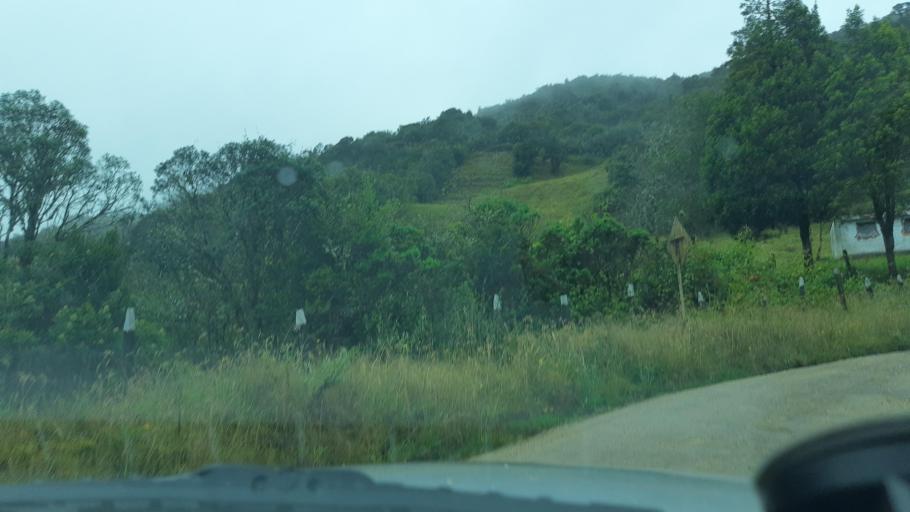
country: CO
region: Cundinamarca
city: Umbita
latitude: 5.2156
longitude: -73.5216
